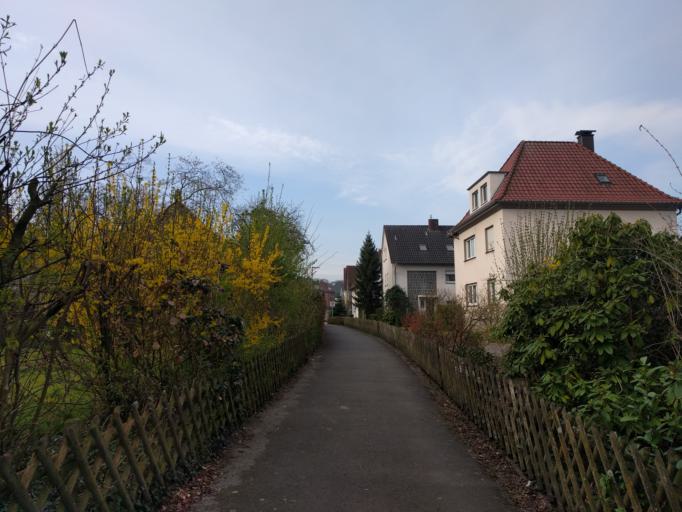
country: DE
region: North Rhine-Westphalia
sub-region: Regierungsbezirk Detmold
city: Bielefeld
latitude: 52.0452
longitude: 8.5111
